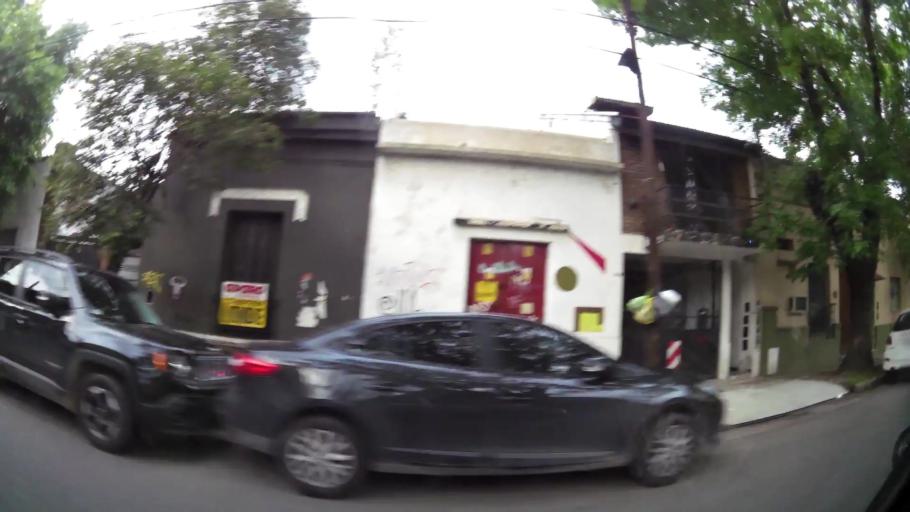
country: AR
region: Buenos Aires
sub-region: Partido de Quilmes
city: Quilmes
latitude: -34.7265
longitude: -58.2515
